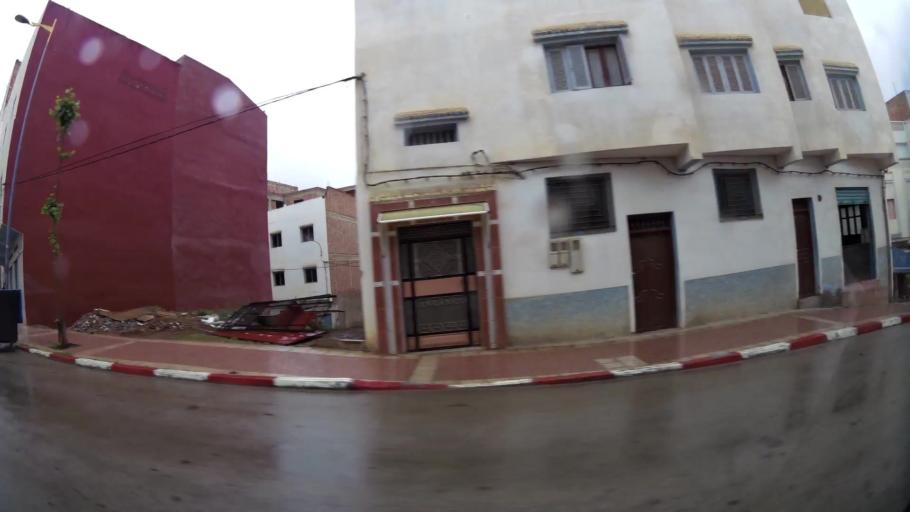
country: MA
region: Taza-Al Hoceima-Taounate
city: Imzourene
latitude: 35.1534
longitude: -3.8489
